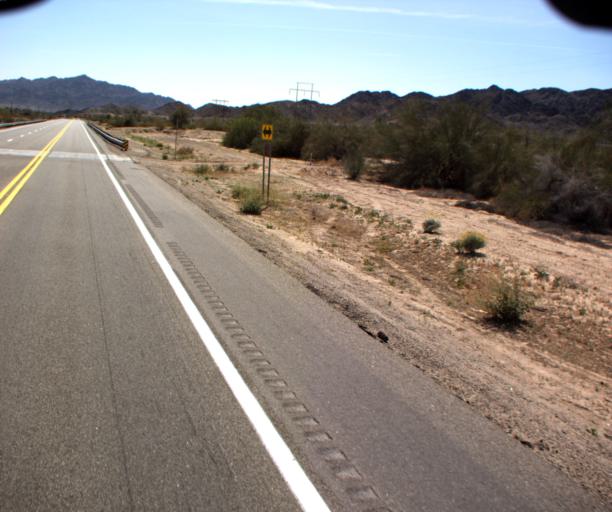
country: US
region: Arizona
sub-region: Yuma County
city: Fortuna Foothills
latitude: 32.8006
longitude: -114.3808
